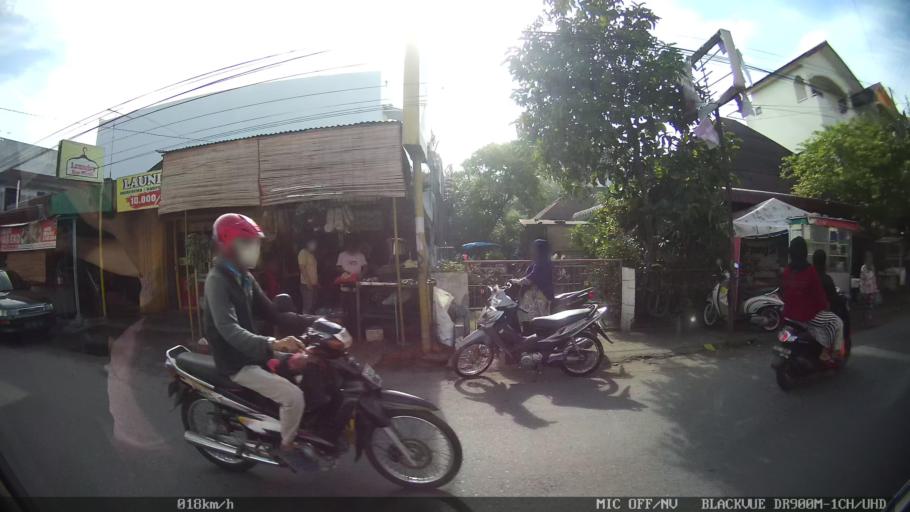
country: ID
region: North Sumatra
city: Medan
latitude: 3.6024
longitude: 98.6649
